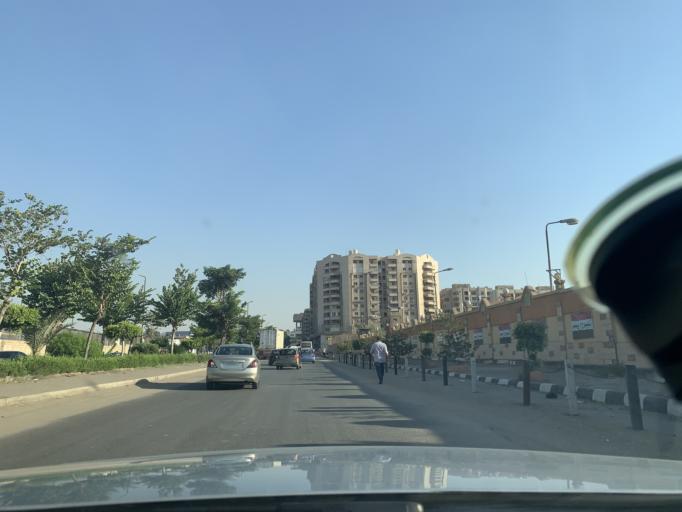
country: EG
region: Muhafazat al Qahirah
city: Cairo
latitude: 30.0403
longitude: 31.3460
